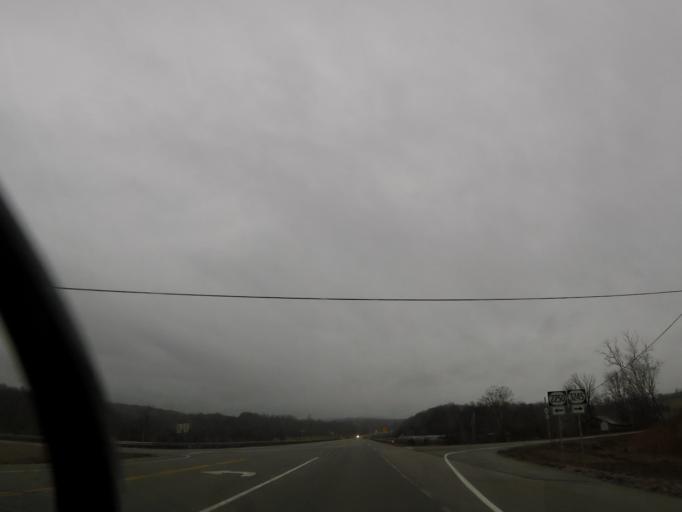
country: US
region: Kentucky
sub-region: Rockcastle County
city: Brodhead
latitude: 37.3909
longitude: -84.4229
